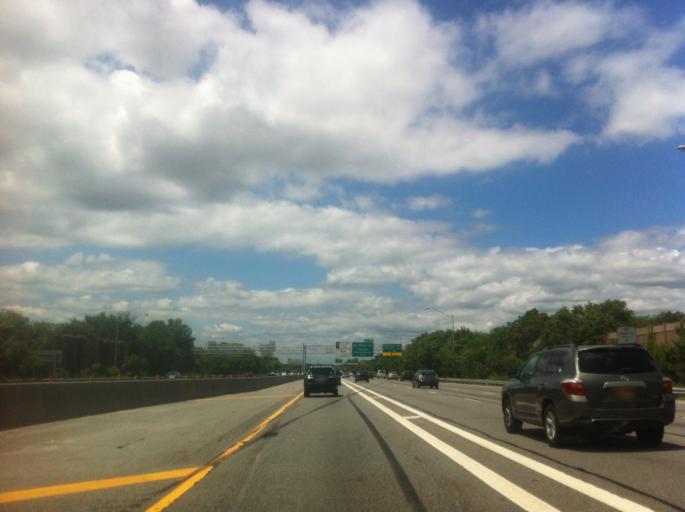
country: US
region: New York
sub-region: Suffolk County
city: Holbrook
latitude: 40.8148
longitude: -73.0947
